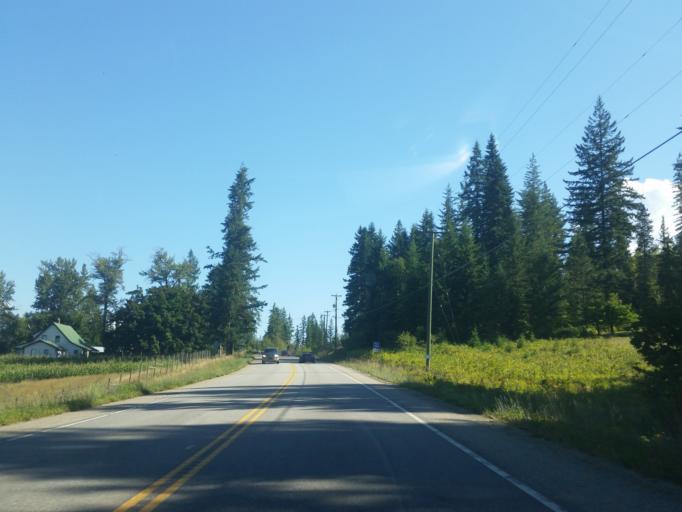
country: CA
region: British Columbia
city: Enderby
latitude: 50.6678
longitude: -119.0643
